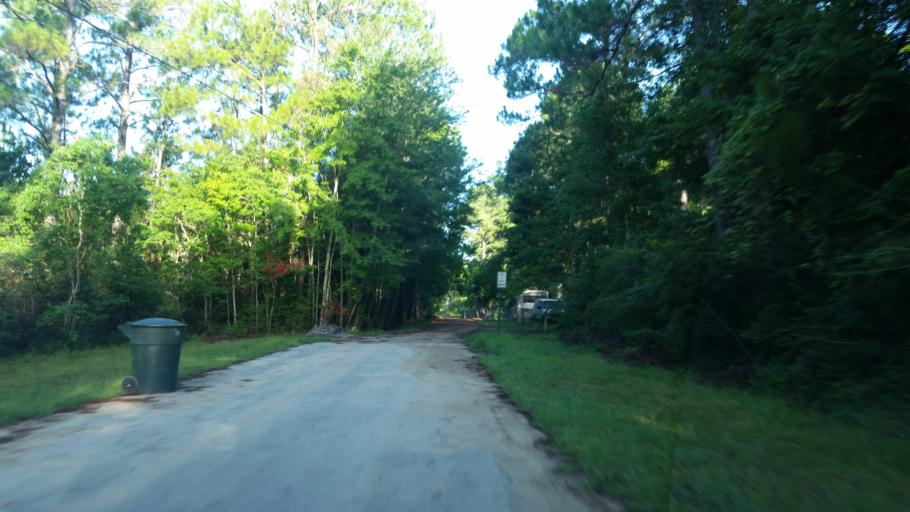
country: US
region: Florida
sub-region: Escambia County
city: Myrtle Grove
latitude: 30.4068
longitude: -87.3298
